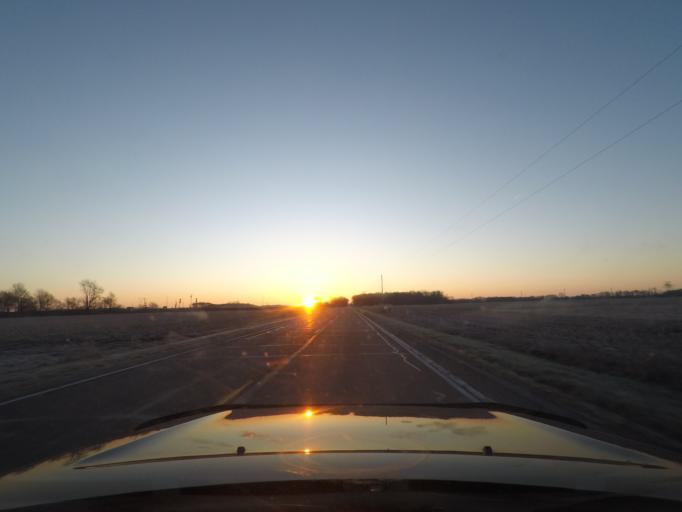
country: US
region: Indiana
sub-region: Saint Joseph County
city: Walkerton
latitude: 41.4763
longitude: -86.5565
